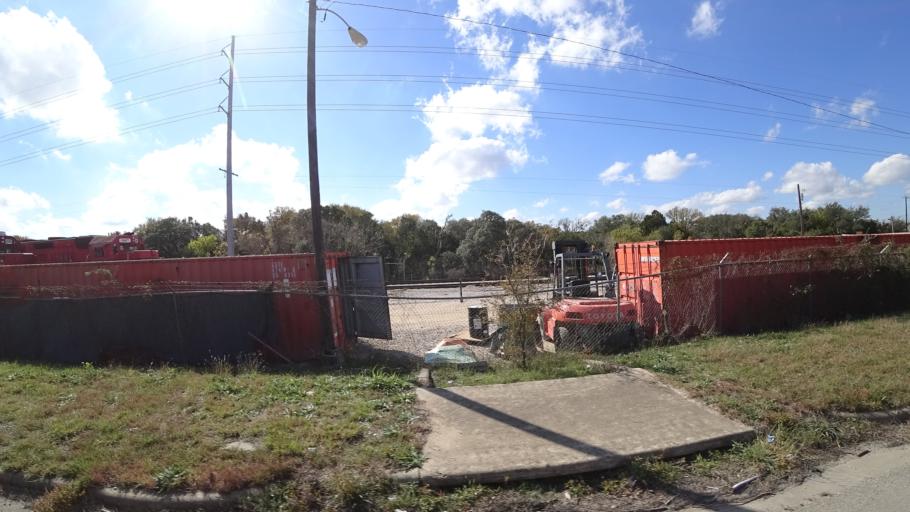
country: US
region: Texas
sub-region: Travis County
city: Wells Branch
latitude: 30.4432
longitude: -97.7070
